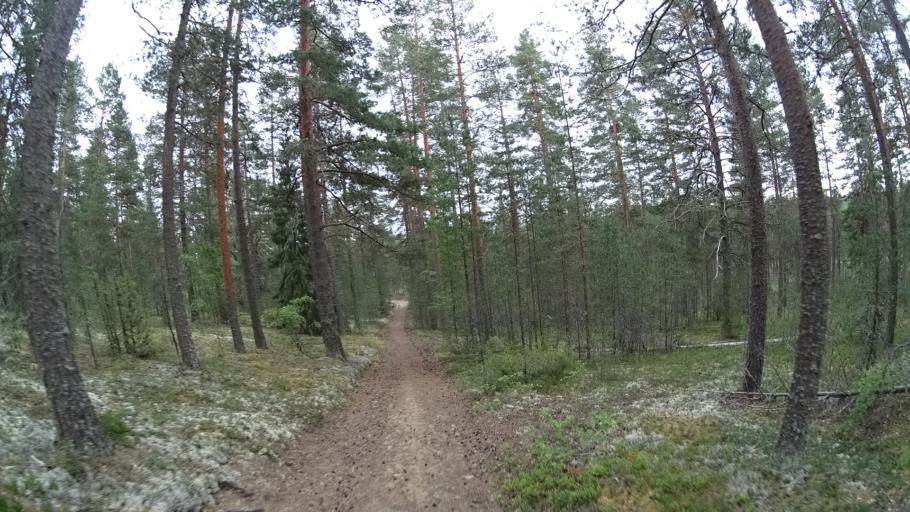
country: FI
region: Satakunta
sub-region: Pohjois-Satakunta
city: Jaemijaervi
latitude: 61.7701
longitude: 22.7433
